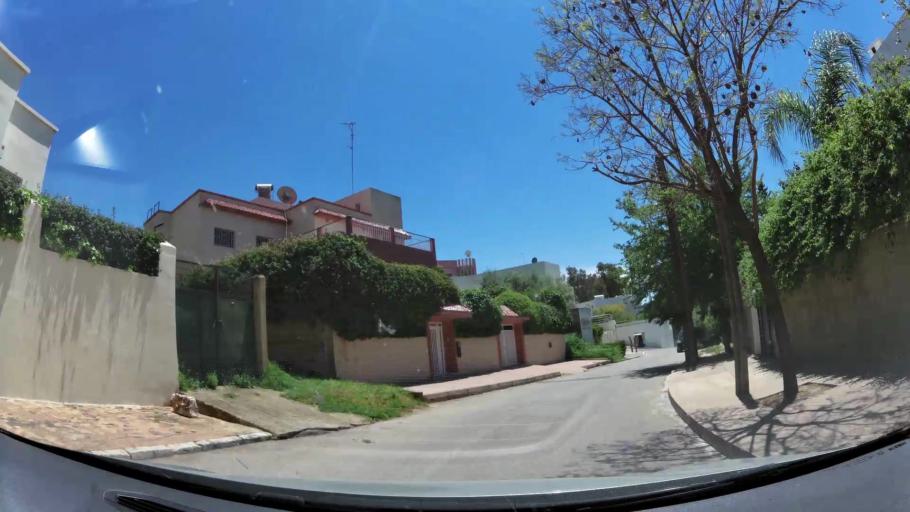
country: MA
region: Meknes-Tafilalet
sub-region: Meknes
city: Meknes
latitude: 33.9096
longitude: -5.5633
